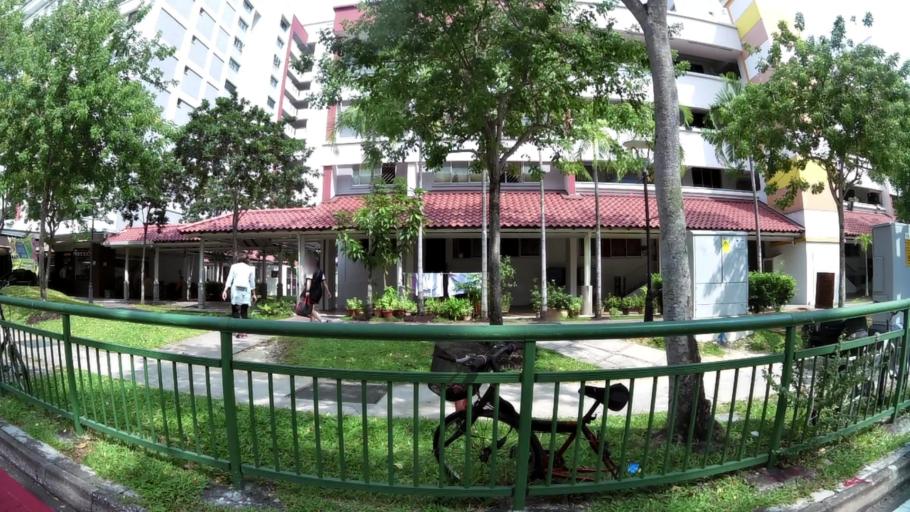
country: SG
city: Singapore
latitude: 1.3576
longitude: 103.9503
